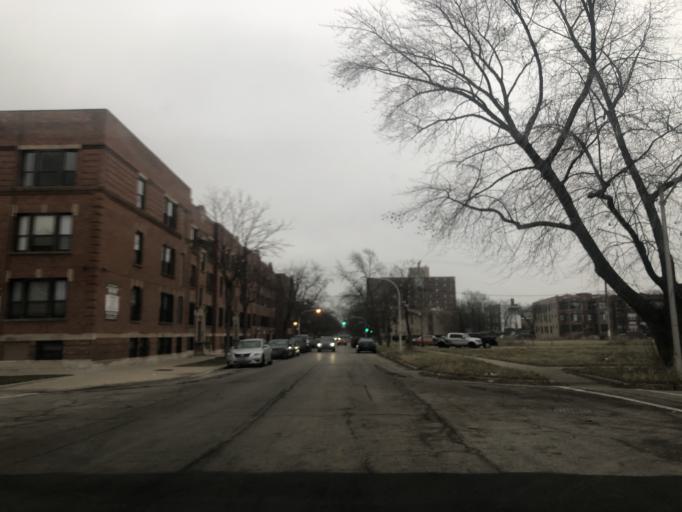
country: US
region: Illinois
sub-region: Cook County
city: Chicago
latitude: 41.7857
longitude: -87.6175
